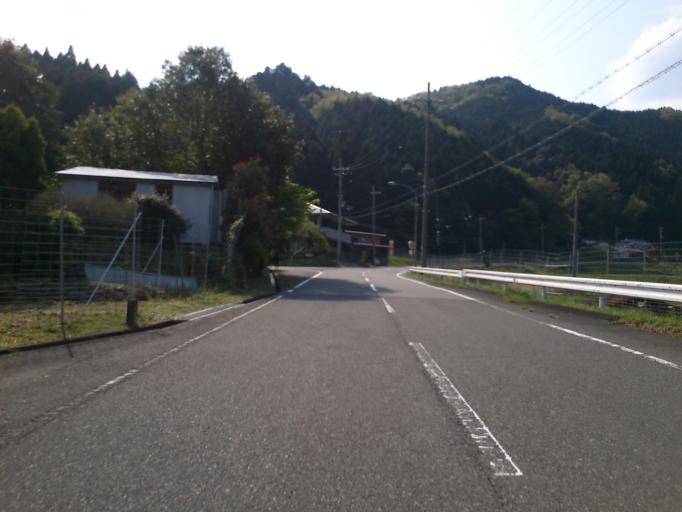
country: JP
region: Kyoto
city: Fukuchiyama
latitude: 35.3469
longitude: 135.0039
